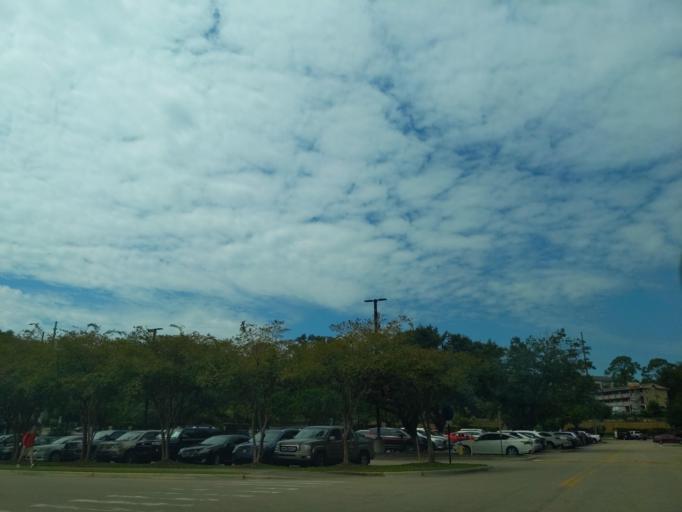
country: US
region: Florida
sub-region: Leon County
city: Tallahassee
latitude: 30.4373
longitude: -84.3030
